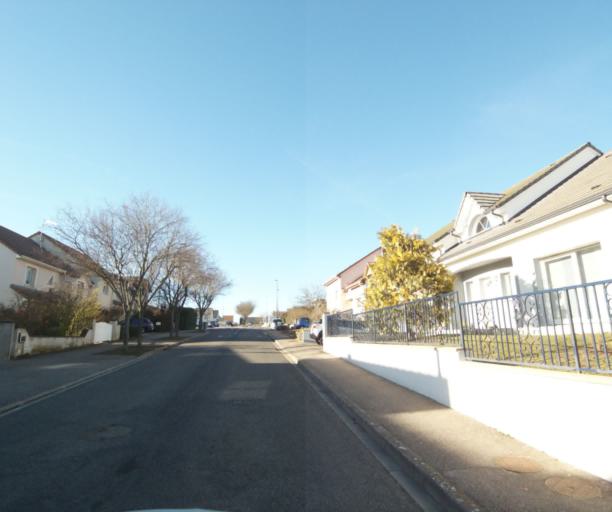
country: FR
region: Lorraine
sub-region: Departement de Meurthe-et-Moselle
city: Heillecourt
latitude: 48.6566
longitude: 6.2190
